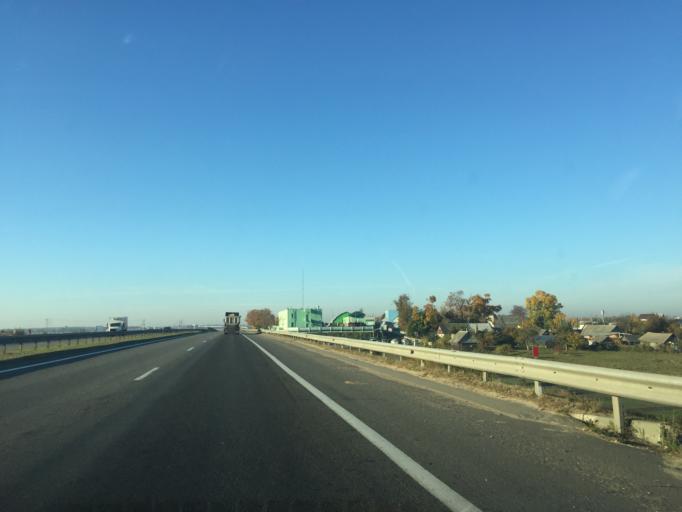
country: BY
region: Minsk
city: Pryvol'ny
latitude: 53.8155
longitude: 27.8166
